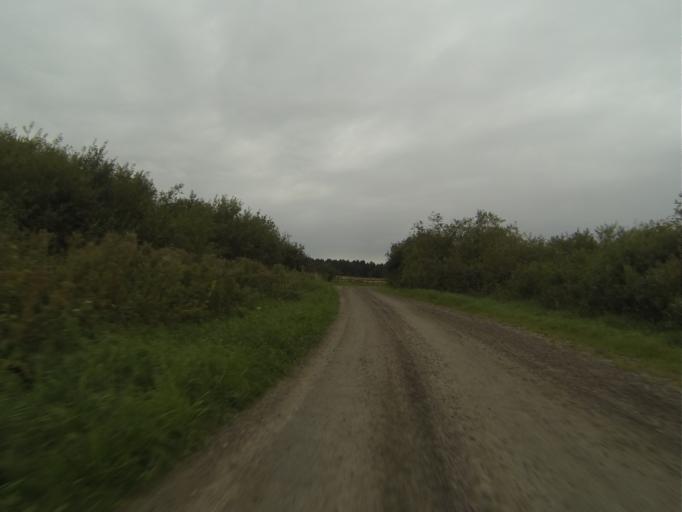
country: SE
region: Skane
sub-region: Lunds Kommun
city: Veberod
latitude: 55.7144
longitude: 13.4142
